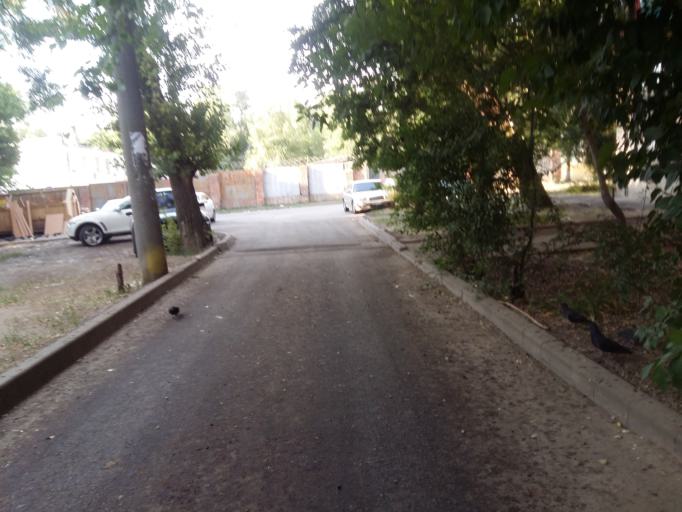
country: RU
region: Rostov
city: Imeni Chkalova
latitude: 47.2763
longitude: 39.7373
